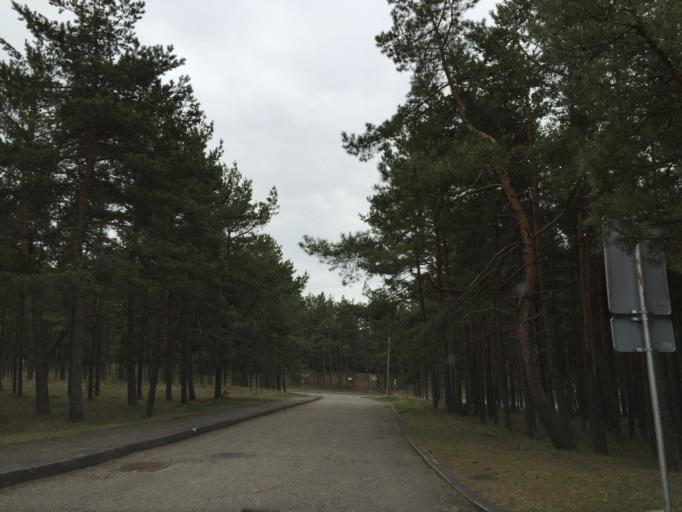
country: LT
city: Nida
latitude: 55.3030
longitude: 20.9972
